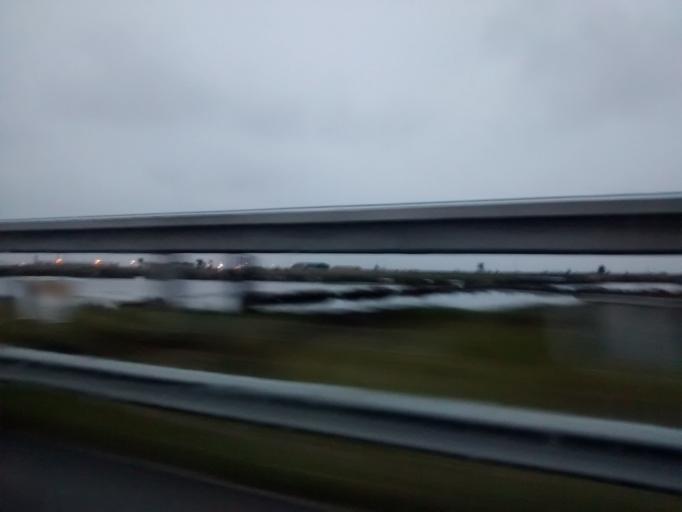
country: PT
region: Aveiro
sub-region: Aveiro
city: Aveiro
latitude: 40.6465
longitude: -8.6541
